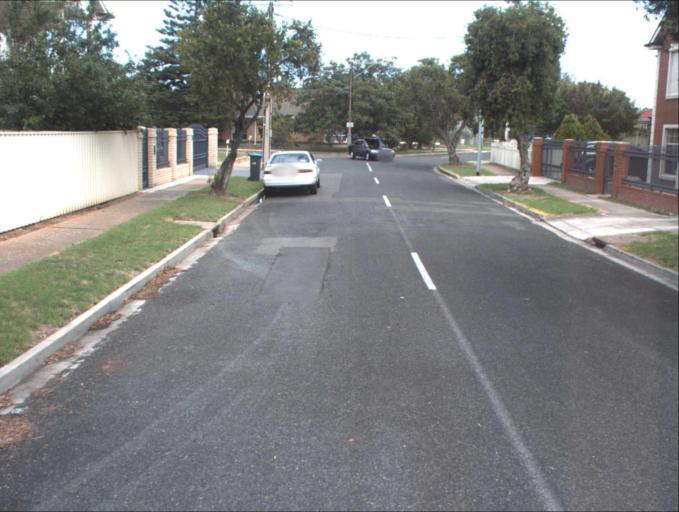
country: AU
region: South Australia
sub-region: Charles Sturt
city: Woodville
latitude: -34.8774
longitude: 138.5604
